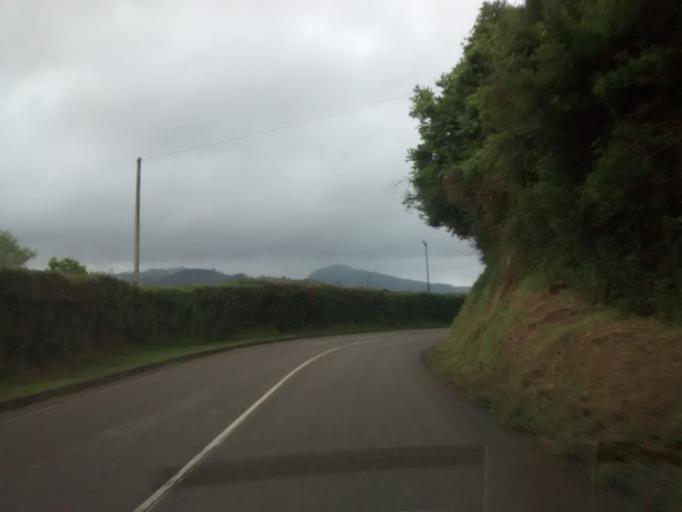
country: ES
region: Asturias
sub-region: Province of Asturias
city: Villaviciosa
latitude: 43.5162
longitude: -5.4063
